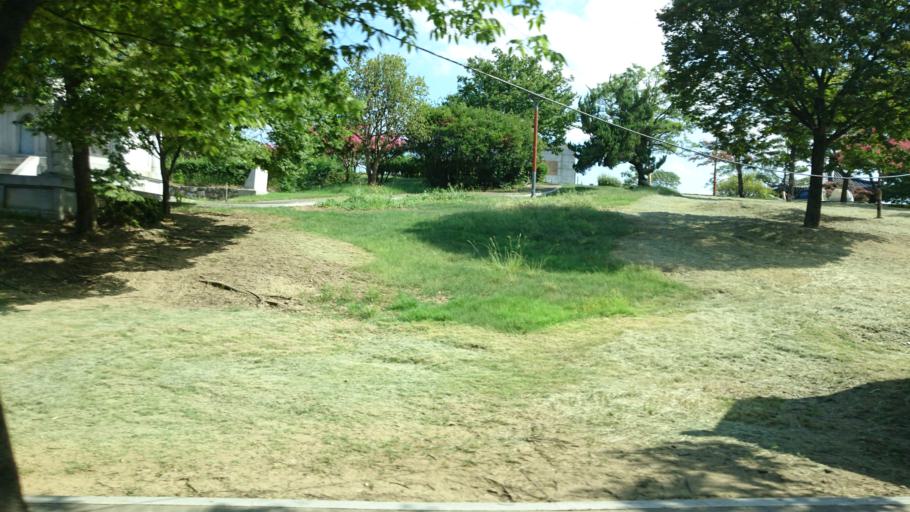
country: KR
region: Daegu
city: Daegu
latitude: 35.8763
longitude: 128.6571
